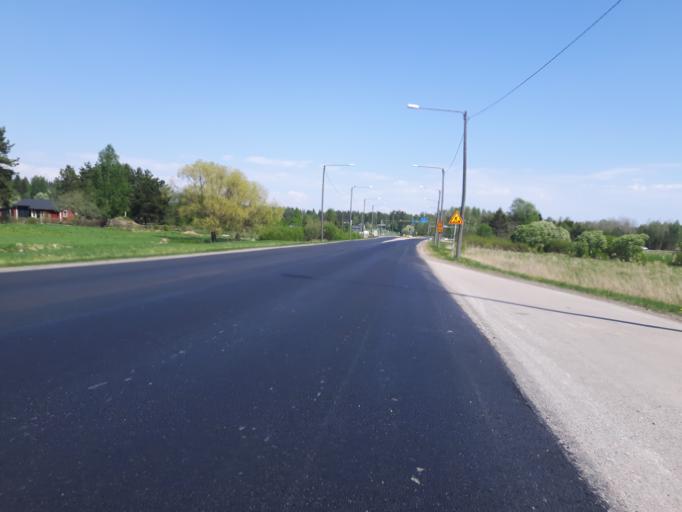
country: FI
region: Uusimaa
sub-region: Helsinki
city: Pornainen
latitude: 60.3392
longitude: 25.4683
